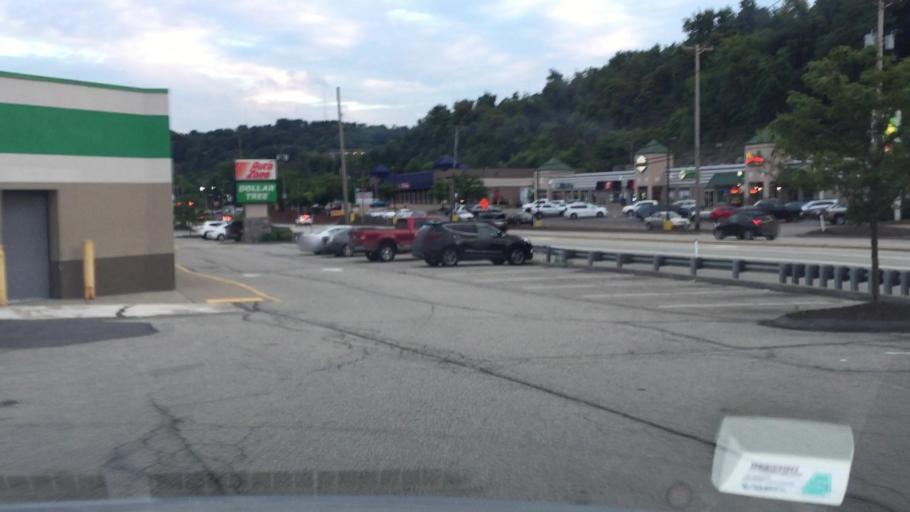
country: US
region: Pennsylvania
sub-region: Allegheny County
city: West View
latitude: 40.5217
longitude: -80.0049
